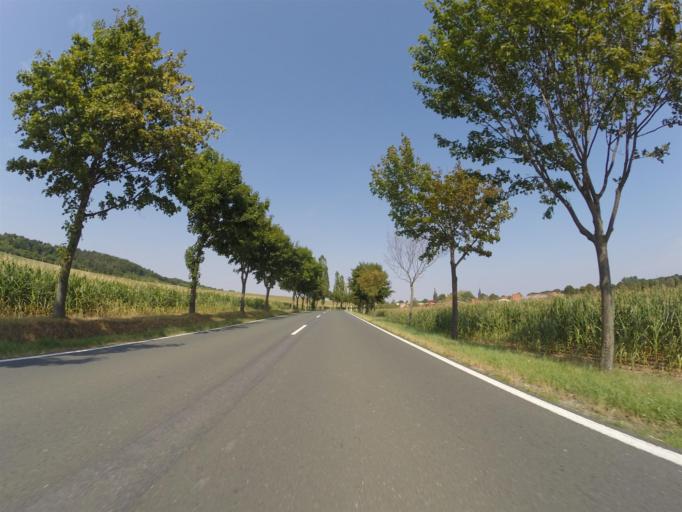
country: DE
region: Thuringia
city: Schongleina
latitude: 50.9050
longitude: 11.7166
